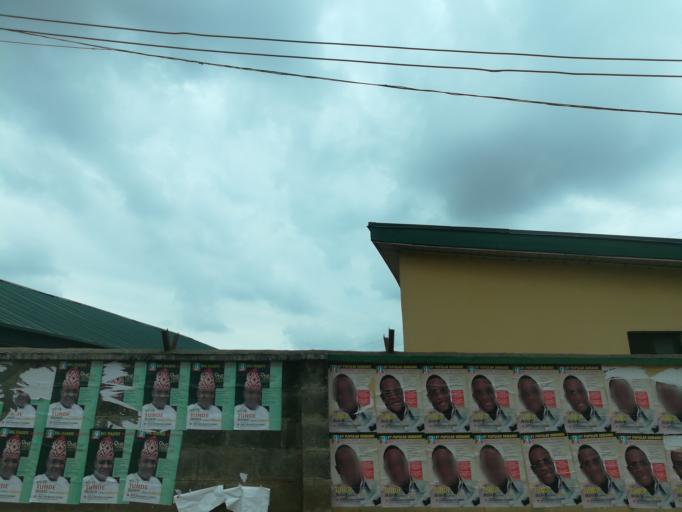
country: NG
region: Lagos
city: Ojota
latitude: 6.6092
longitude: 3.3985
